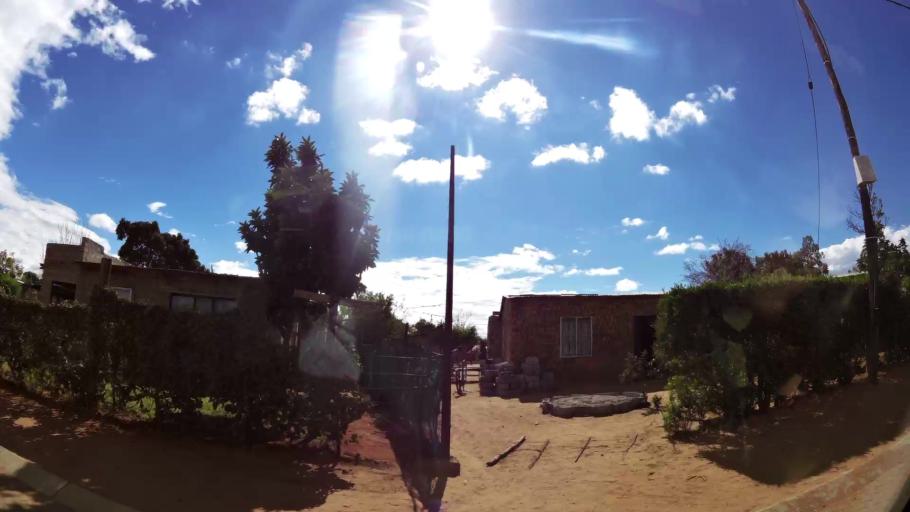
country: ZA
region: Limpopo
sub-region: Waterberg District Municipality
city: Bela-Bela
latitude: -24.8810
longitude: 28.3298
